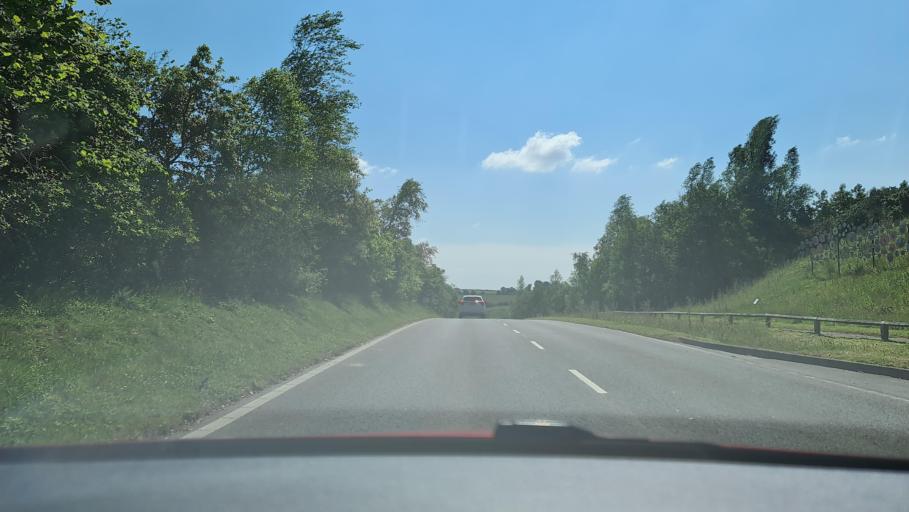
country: GB
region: England
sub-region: Cornwall
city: St Austell
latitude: 50.3593
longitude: -4.7472
